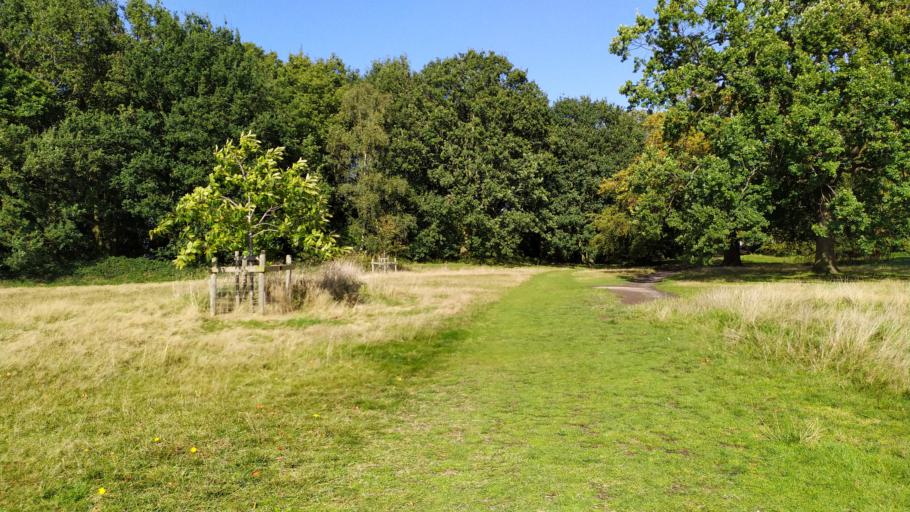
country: GB
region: England
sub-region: City and Borough of Leeds
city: Horsforth
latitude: 53.8243
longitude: -1.5953
